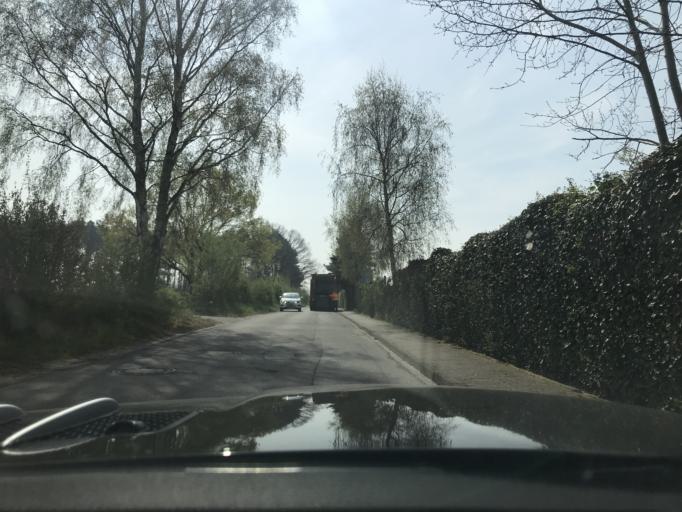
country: DE
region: Schleswig-Holstein
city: Gromitz
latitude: 54.1578
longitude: 10.9895
